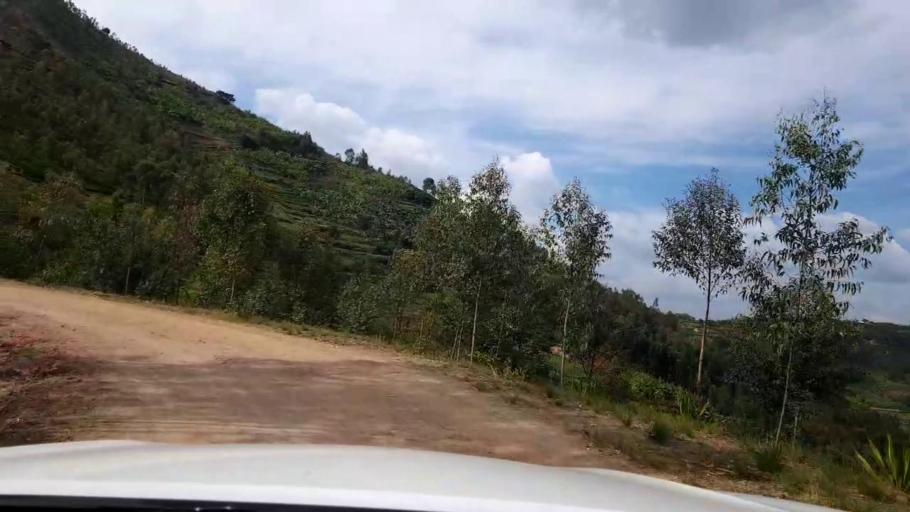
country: RW
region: Southern Province
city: Gitarama
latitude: -1.9935
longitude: 29.7085
